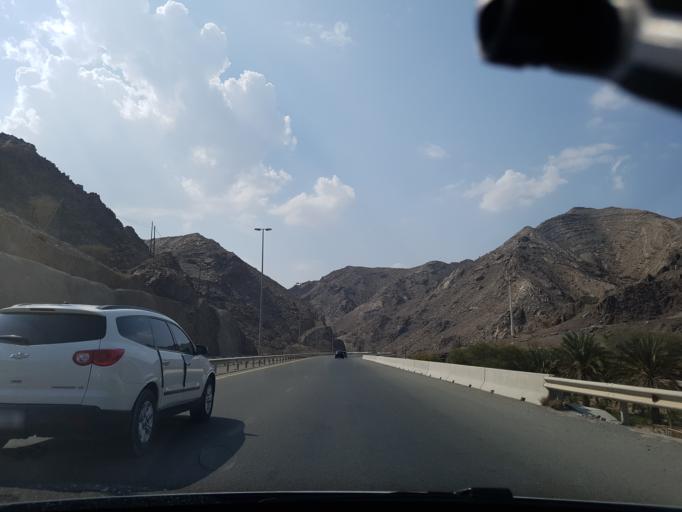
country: AE
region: Al Fujayrah
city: Dibba Al-Fujairah
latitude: 25.5337
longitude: 56.1294
